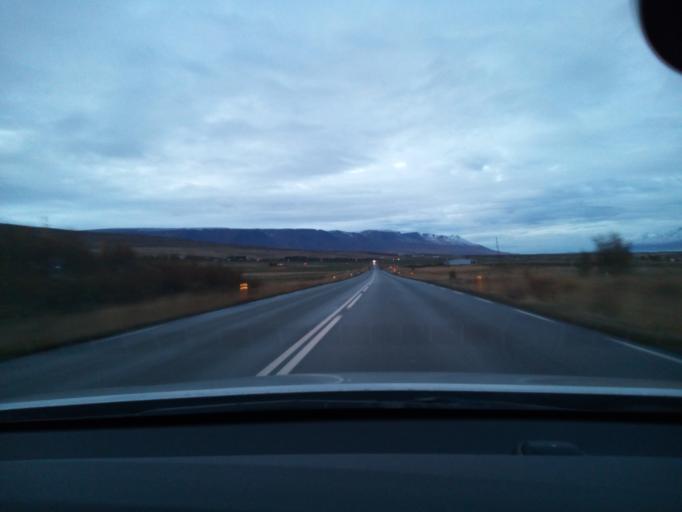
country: IS
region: Northeast
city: Akureyri
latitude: 65.7082
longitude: -18.1594
